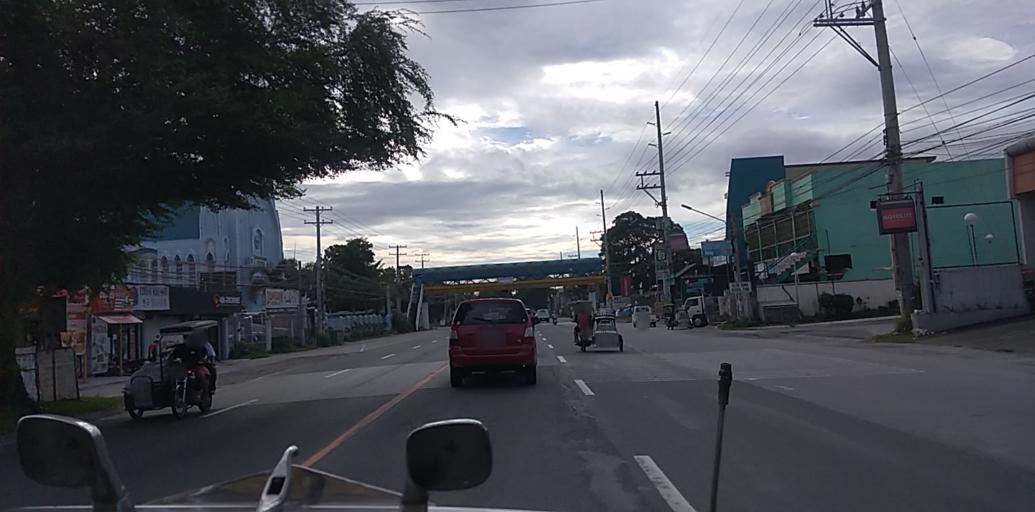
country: PH
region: Central Luzon
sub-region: Province of Pampanga
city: Telabastagan
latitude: 15.0939
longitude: 120.6266
